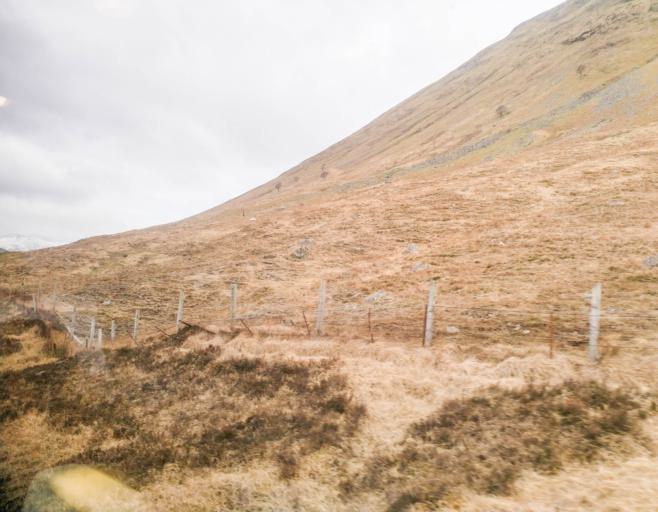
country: GB
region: Scotland
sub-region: Argyll and Bute
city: Garelochhead
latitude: 56.4889
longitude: -4.7263
